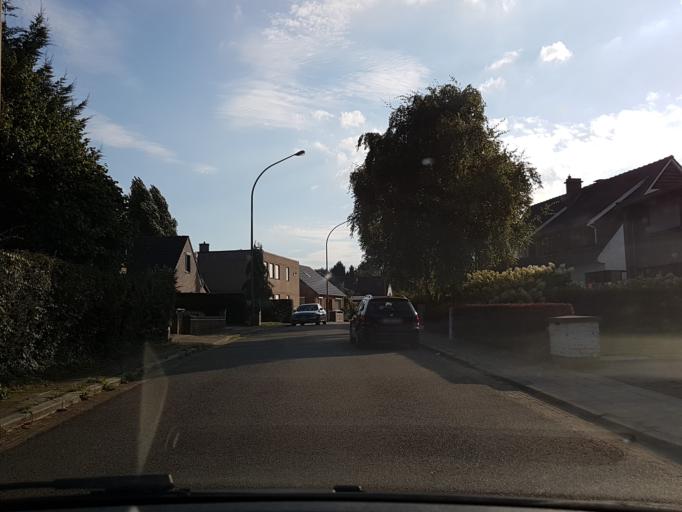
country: BE
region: Flanders
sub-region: Provincie Vlaams-Brabant
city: Leuven
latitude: 50.8894
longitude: 4.6895
